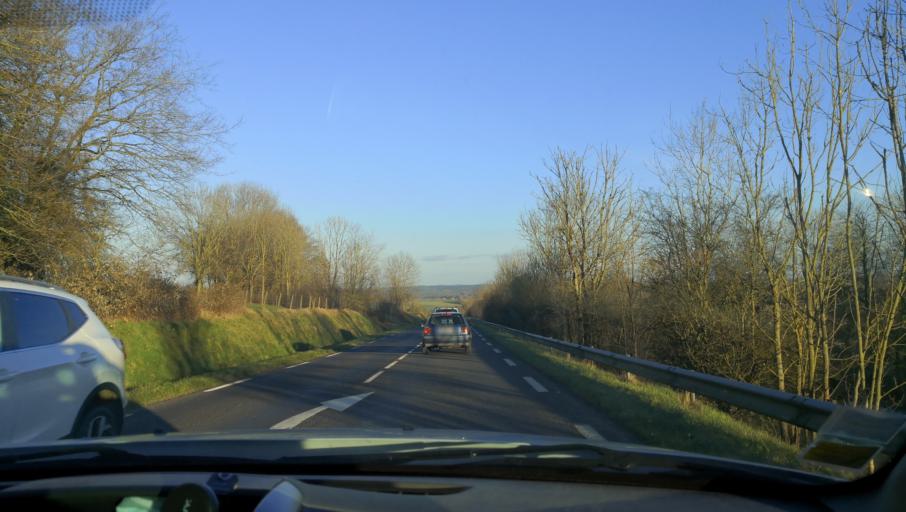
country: FR
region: Haute-Normandie
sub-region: Departement de la Seine-Maritime
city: Buchy
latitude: 49.5936
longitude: 1.4452
